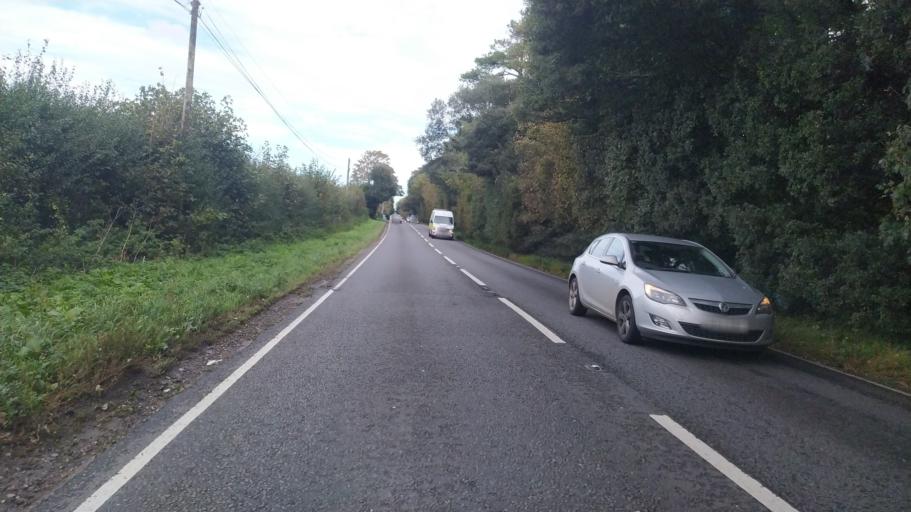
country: GB
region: England
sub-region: Dorset
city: Dorchester
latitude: 50.7231
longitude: -2.4110
